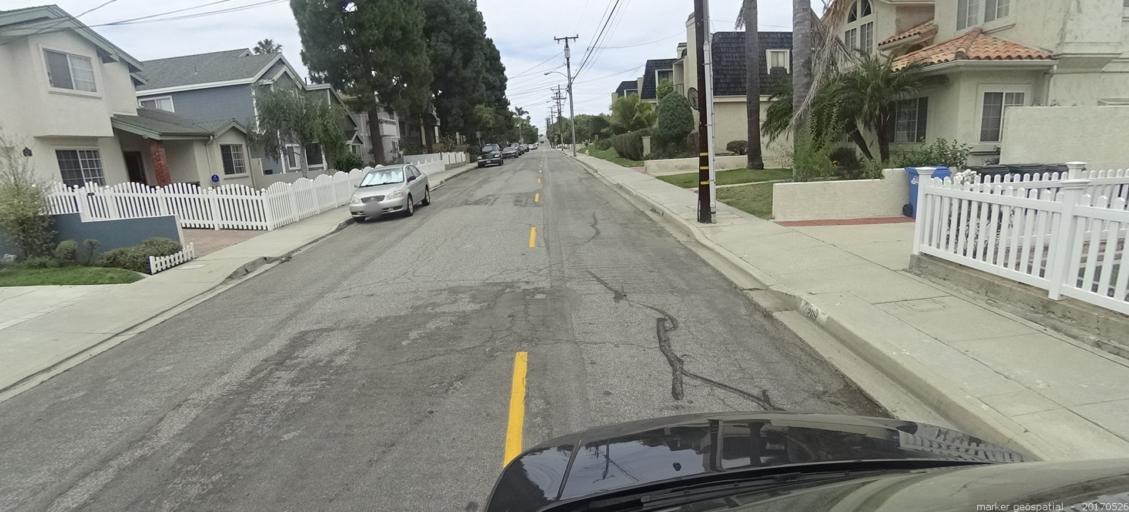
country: US
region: California
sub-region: Los Angeles County
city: Lawndale
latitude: 33.8837
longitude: -118.3732
